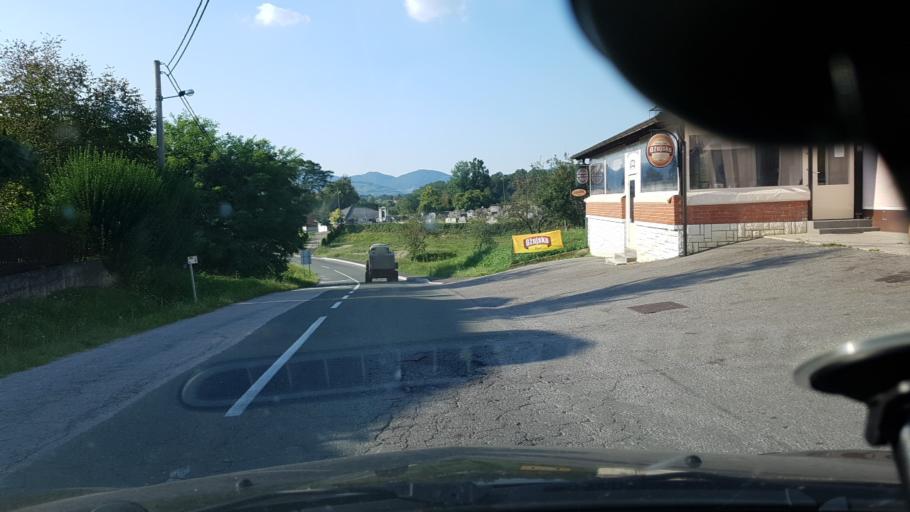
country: SI
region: Bistrica ob Sotli
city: Bistrica ob Sotli
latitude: 45.9854
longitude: 15.7275
